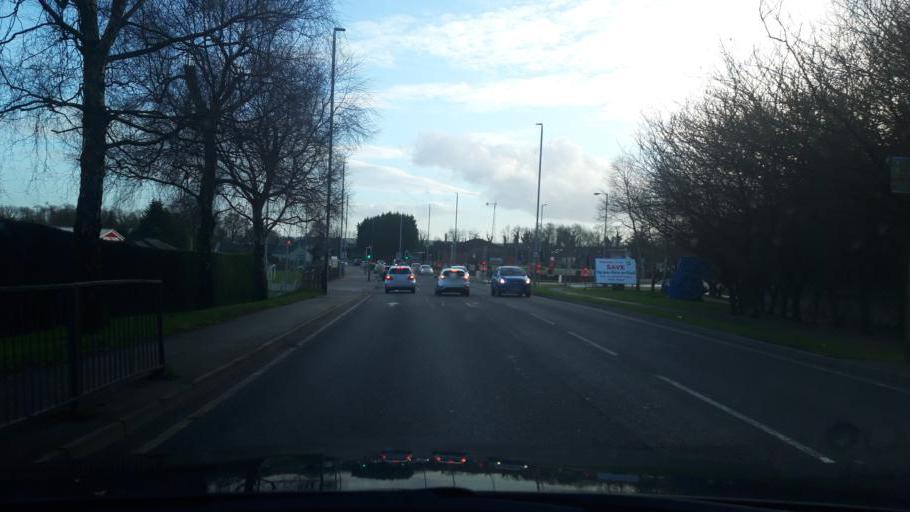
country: GB
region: Northern Ireland
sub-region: Dungannon District
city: Dungannon
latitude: 54.4897
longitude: -6.7481
